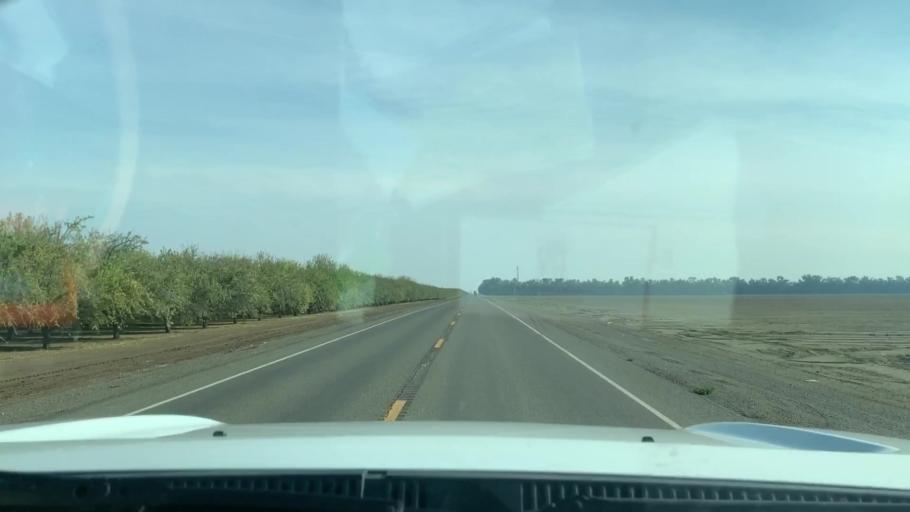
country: US
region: California
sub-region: Fresno County
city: Huron
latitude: 36.2552
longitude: -120.1776
